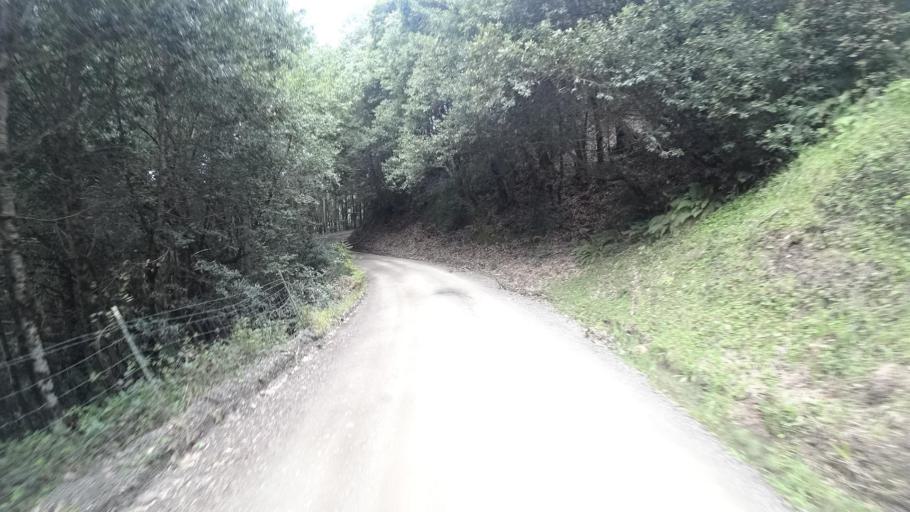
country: US
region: California
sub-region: Humboldt County
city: Blue Lake
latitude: 40.7650
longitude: -123.9546
